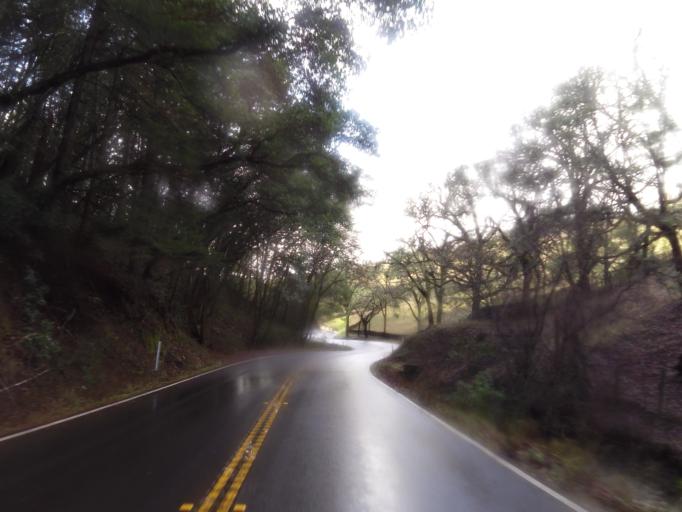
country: US
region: California
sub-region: Sonoma County
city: Cloverdale
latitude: 38.8867
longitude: -123.1226
